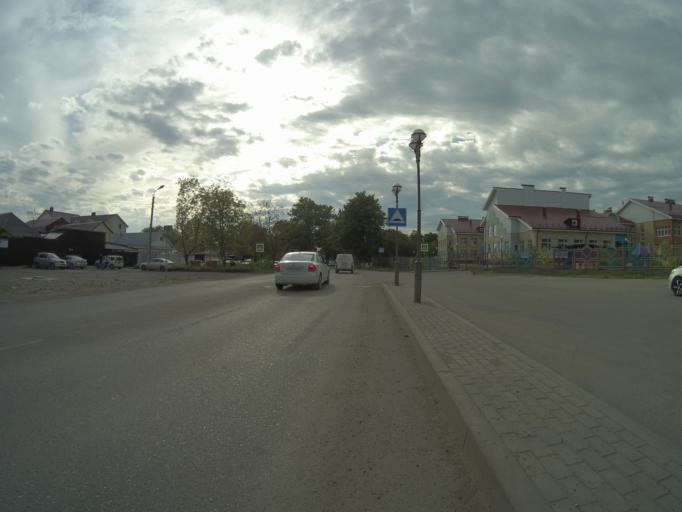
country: RU
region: Stavropol'skiy
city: Svobody
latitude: 44.0396
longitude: 43.0176
